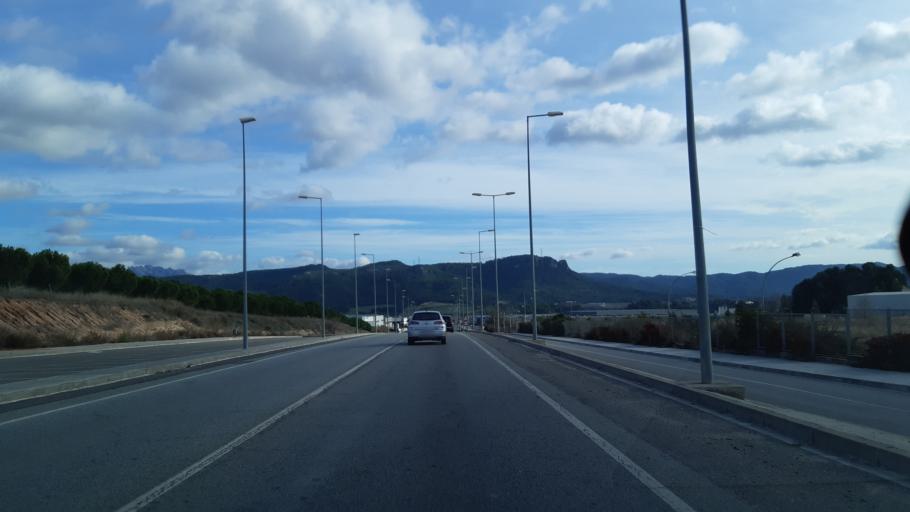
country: ES
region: Catalonia
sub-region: Provincia de Barcelona
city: Vilanova del Cami
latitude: 41.5784
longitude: 1.6456
